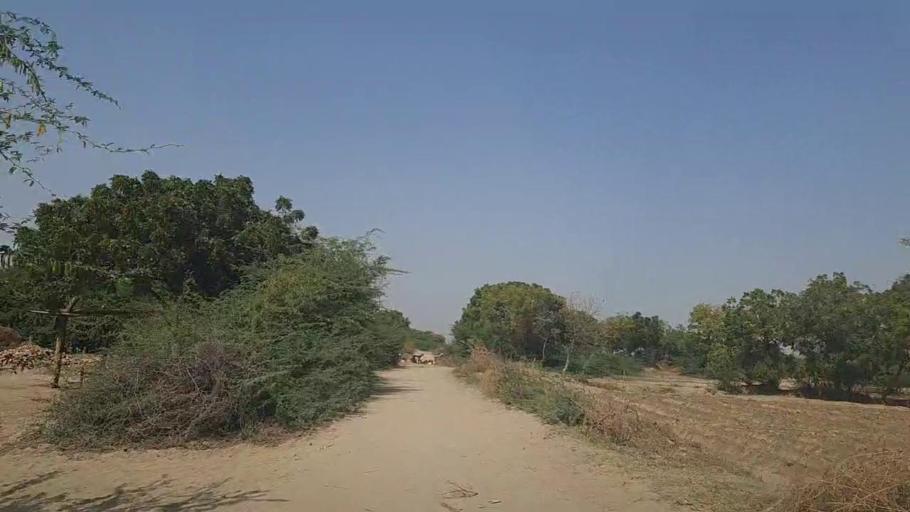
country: PK
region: Sindh
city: Naukot
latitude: 24.8495
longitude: 69.4395
